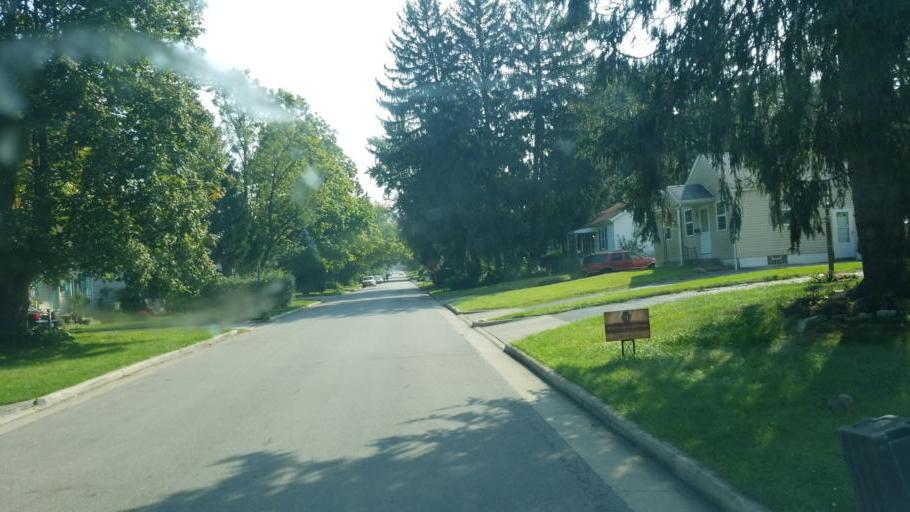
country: US
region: Ohio
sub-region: Franklin County
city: Worthington
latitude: 40.0713
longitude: -83.0239
